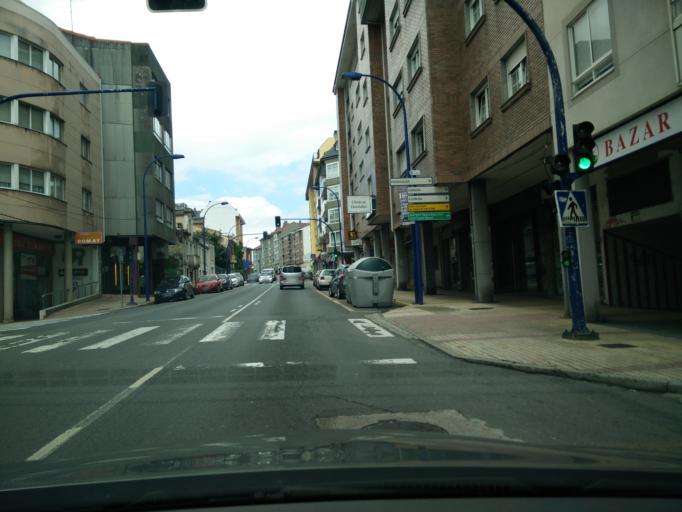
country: ES
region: Galicia
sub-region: Provincia da Coruna
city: Culleredo
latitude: 43.3153
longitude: -8.3834
